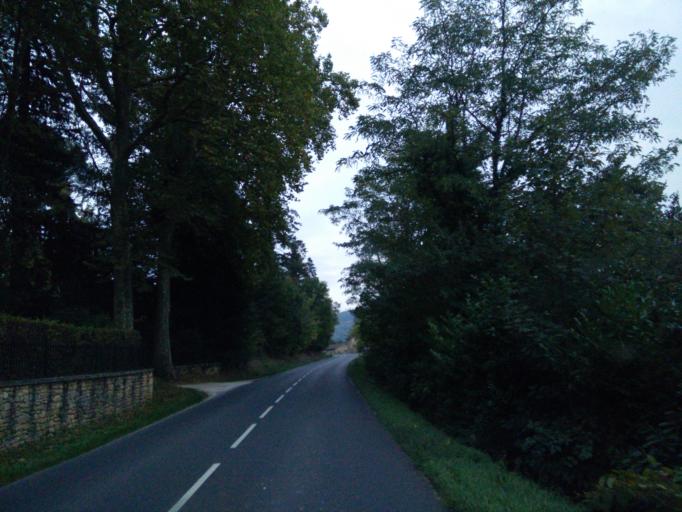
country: FR
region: Aquitaine
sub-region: Departement de la Dordogne
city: Carsac-Aillac
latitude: 44.8352
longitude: 1.2748
